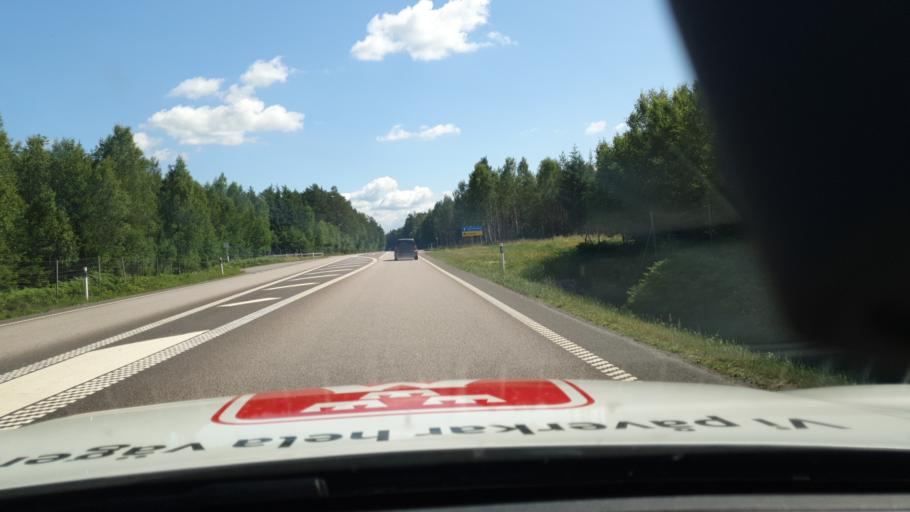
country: SE
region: Vaestra Goetaland
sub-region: Lidkopings Kommun
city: Lidkoping
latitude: 58.4762
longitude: 13.2054
